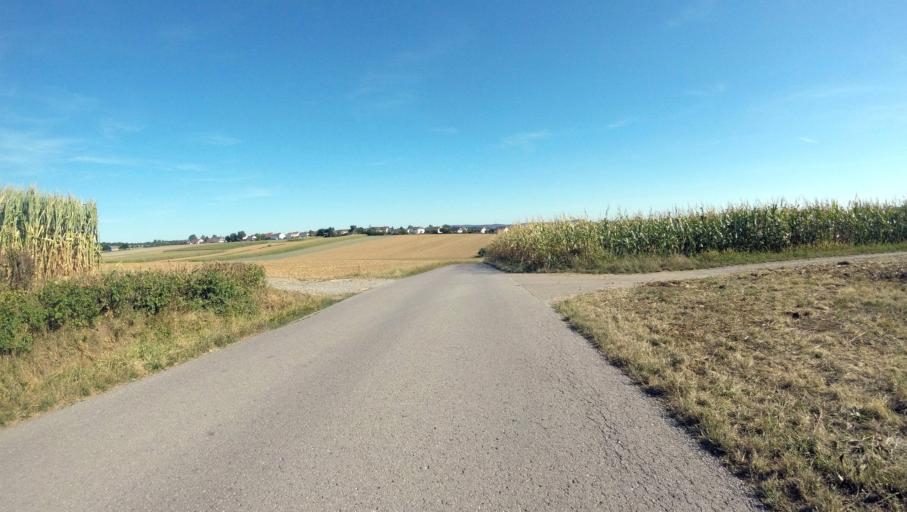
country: DE
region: Baden-Wuerttemberg
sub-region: Regierungsbezirk Stuttgart
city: Kirchberg an der Murr
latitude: 48.9494
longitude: 9.3384
